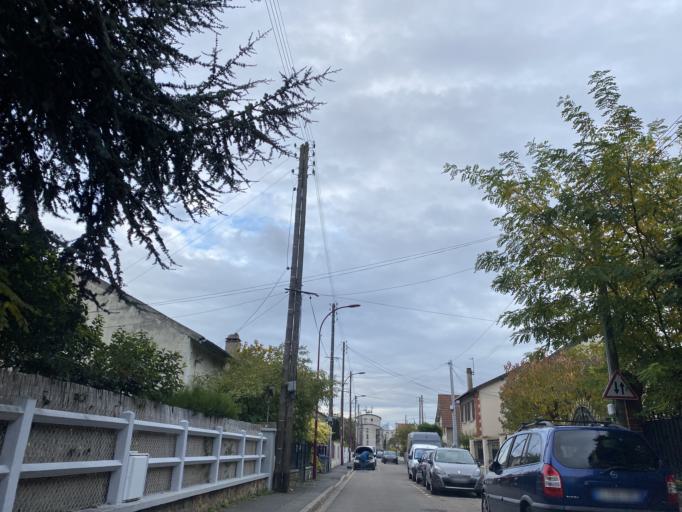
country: FR
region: Ile-de-France
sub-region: Departement du Val-d'Oise
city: Bezons
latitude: 48.9263
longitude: 2.2051
